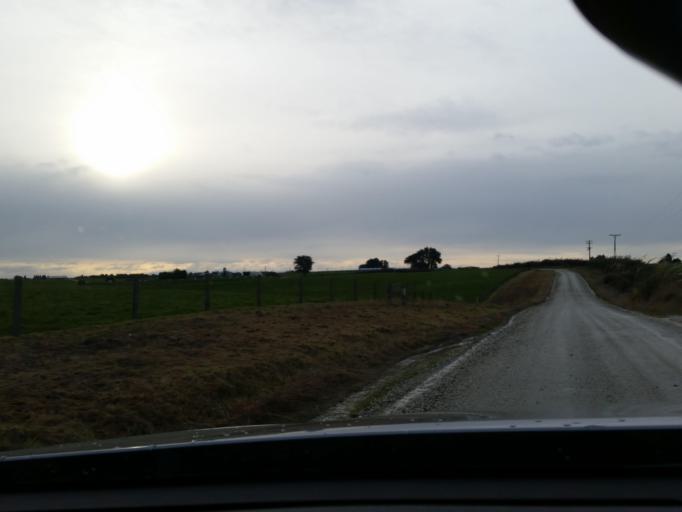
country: NZ
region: Southland
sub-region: Invercargill City
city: Invercargill
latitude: -46.4322
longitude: 168.5386
